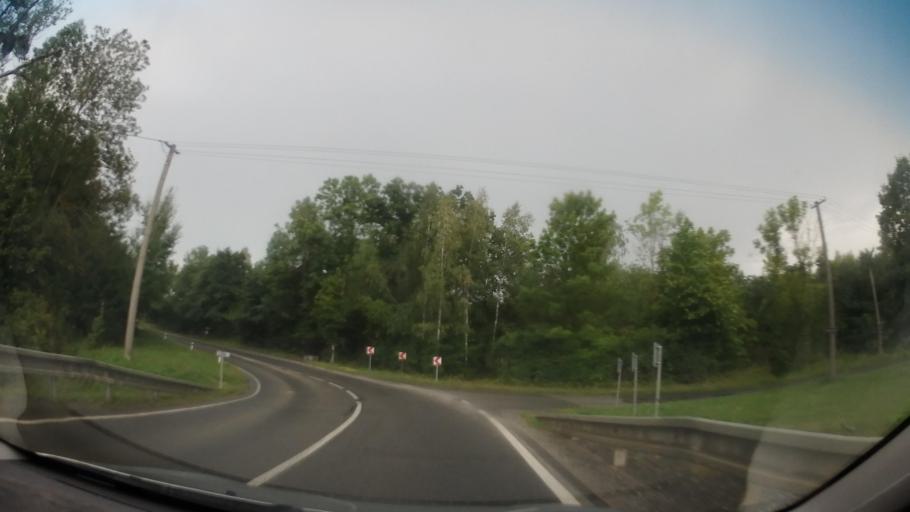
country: CZ
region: Olomoucky
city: Bila Lhota
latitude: 49.7042
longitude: 16.9965
